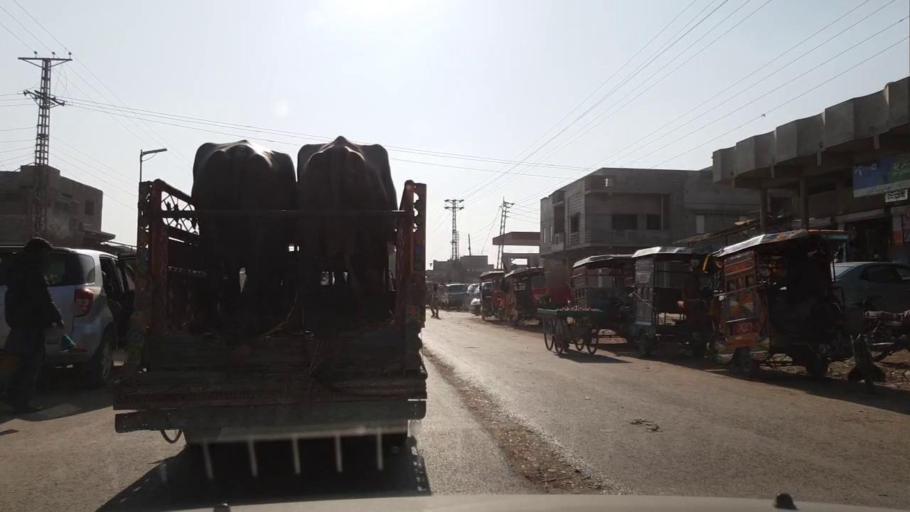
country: PK
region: Sindh
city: Tando Muhammad Khan
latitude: 25.1169
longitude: 68.5355
